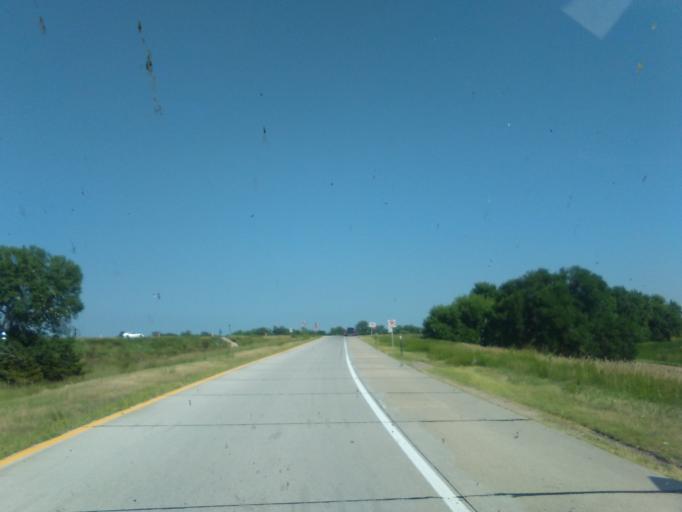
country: US
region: Nebraska
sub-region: Hall County
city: Grand Island
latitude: 40.8190
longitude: -98.3802
